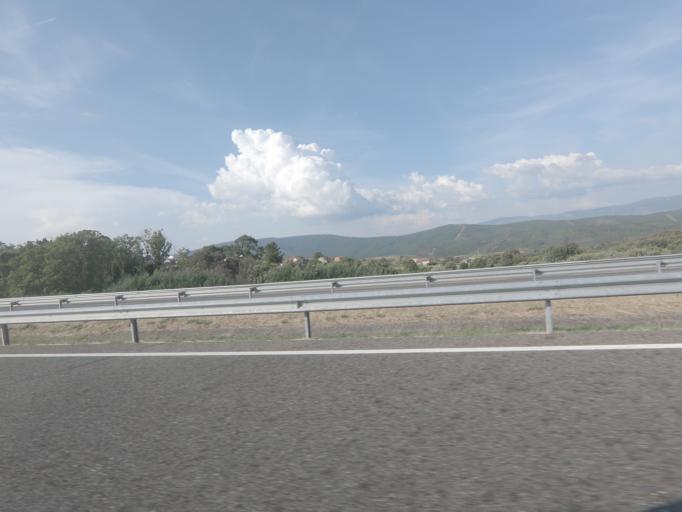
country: ES
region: Galicia
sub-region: Provincia de Ourense
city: Cualedro
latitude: 41.9666
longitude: -7.5288
